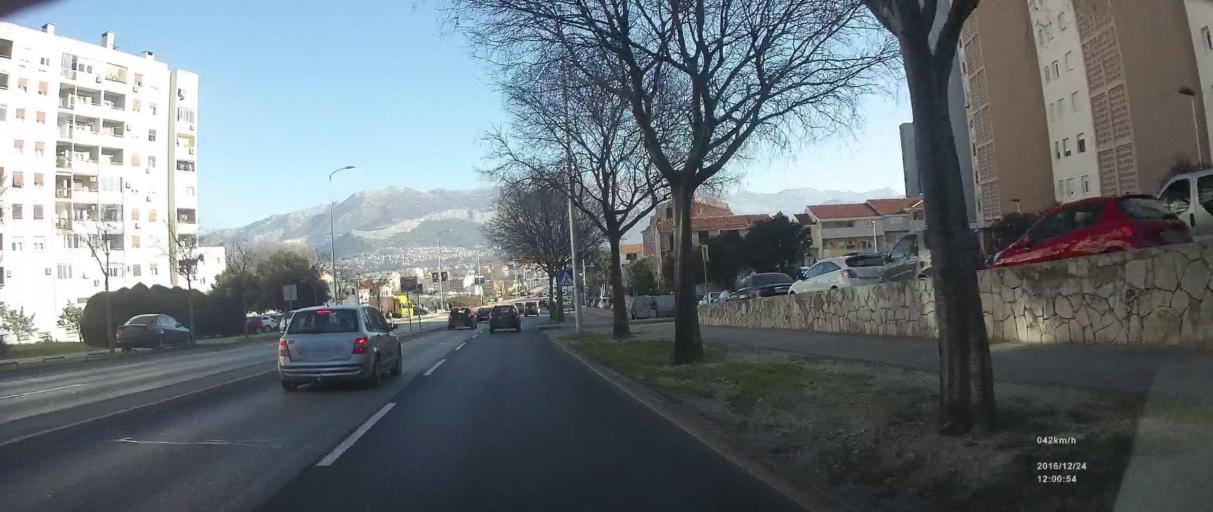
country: HR
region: Splitsko-Dalmatinska
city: Vranjic
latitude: 43.5155
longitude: 16.4776
